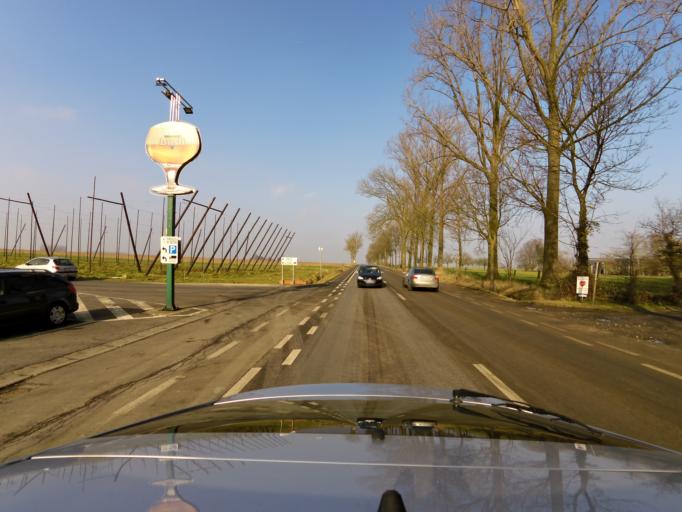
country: BE
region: Wallonia
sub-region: Province du Hainaut
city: Peruwelz
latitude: 50.5770
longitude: 3.5567
